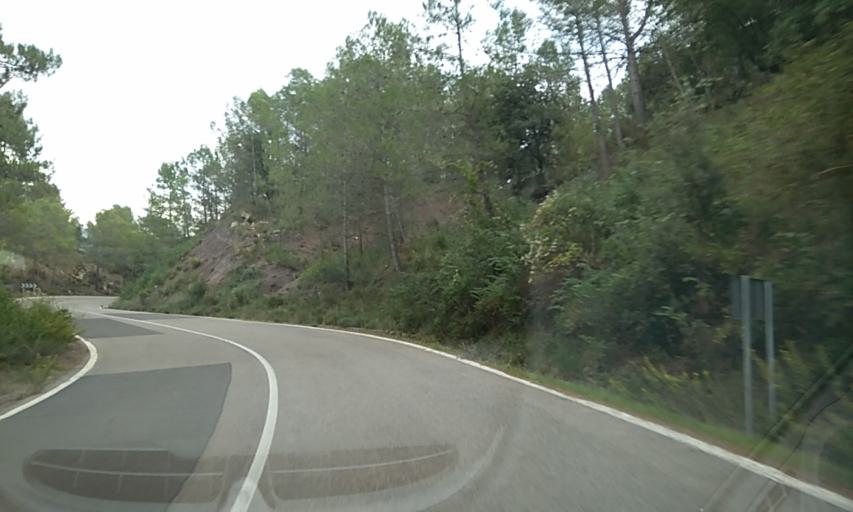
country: ES
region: Valencia
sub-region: Provincia de Castello
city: Puebla de Arenoso
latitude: 40.0878
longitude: -0.5674
